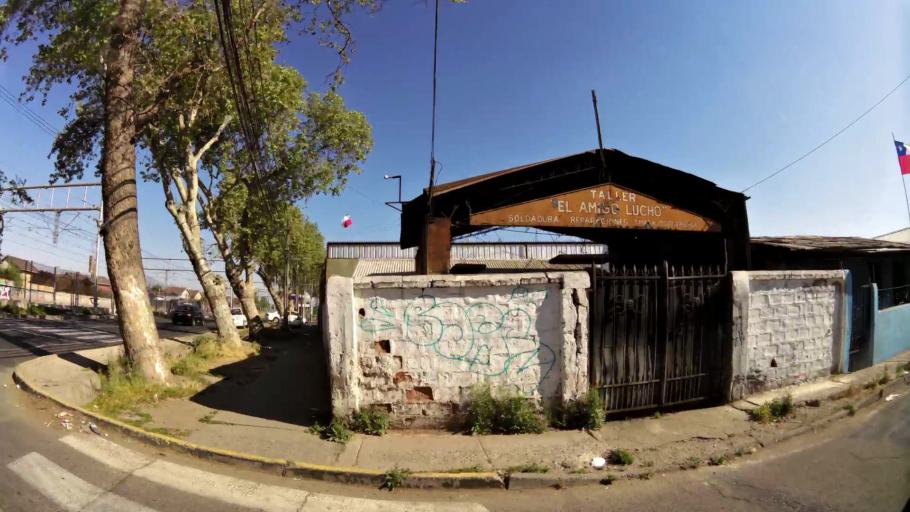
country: CL
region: Santiago Metropolitan
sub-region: Provincia de Maipo
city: San Bernardo
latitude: -33.6102
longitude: -70.6971
